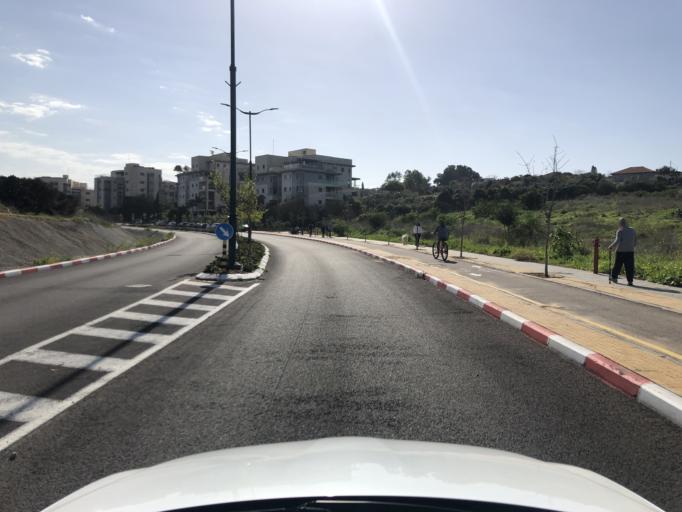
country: IL
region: Central District
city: Ness Ziona
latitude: 31.9172
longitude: 34.7857
